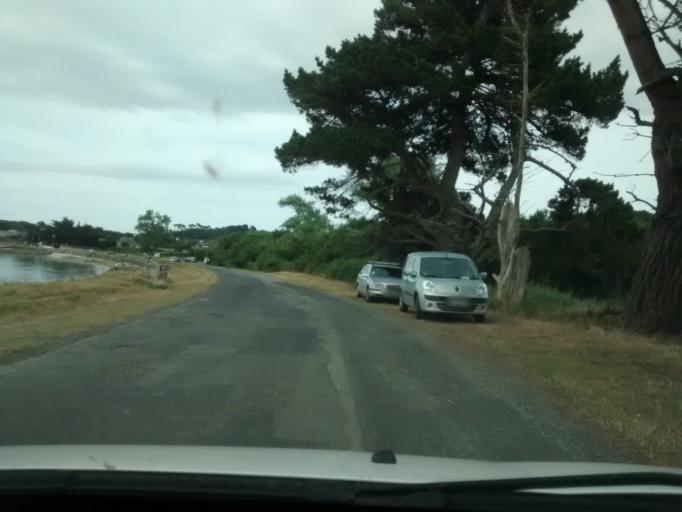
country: FR
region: Brittany
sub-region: Departement des Cotes-d'Armor
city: Plougrescant
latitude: 48.8340
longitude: -3.2651
